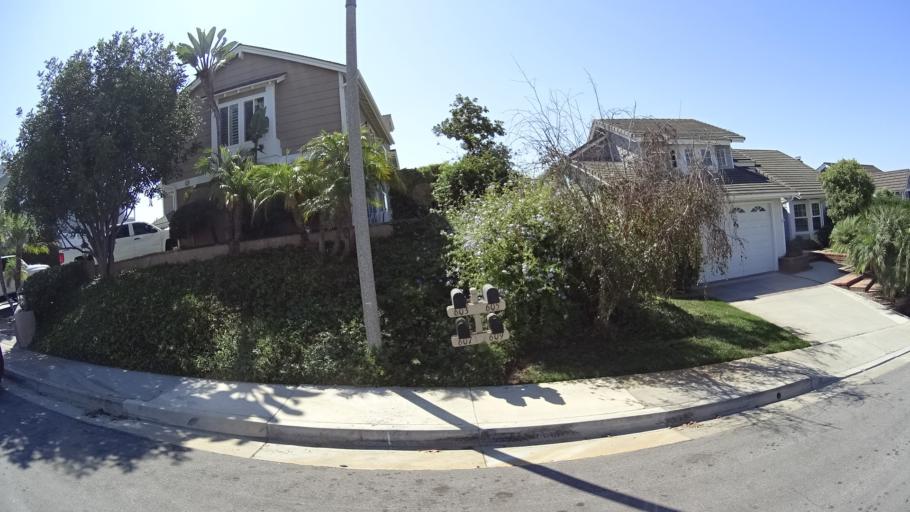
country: US
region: California
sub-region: Orange County
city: San Clemente
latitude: 33.4564
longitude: -117.6360
